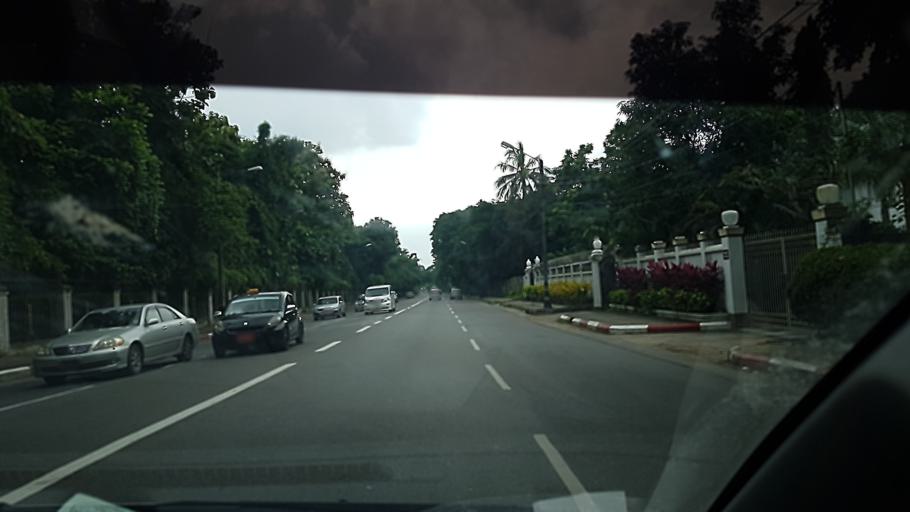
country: MM
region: Yangon
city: Yangon
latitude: 16.7909
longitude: 96.1335
